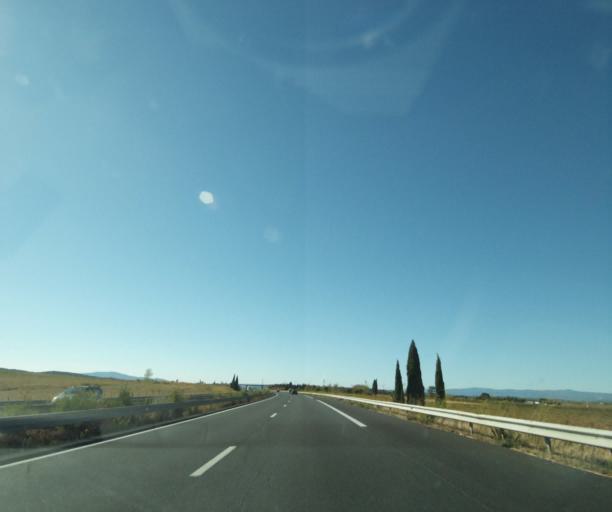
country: FR
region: Languedoc-Roussillon
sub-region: Departement de l'Aude
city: Ornaisons
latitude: 43.1668
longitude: 2.8371
